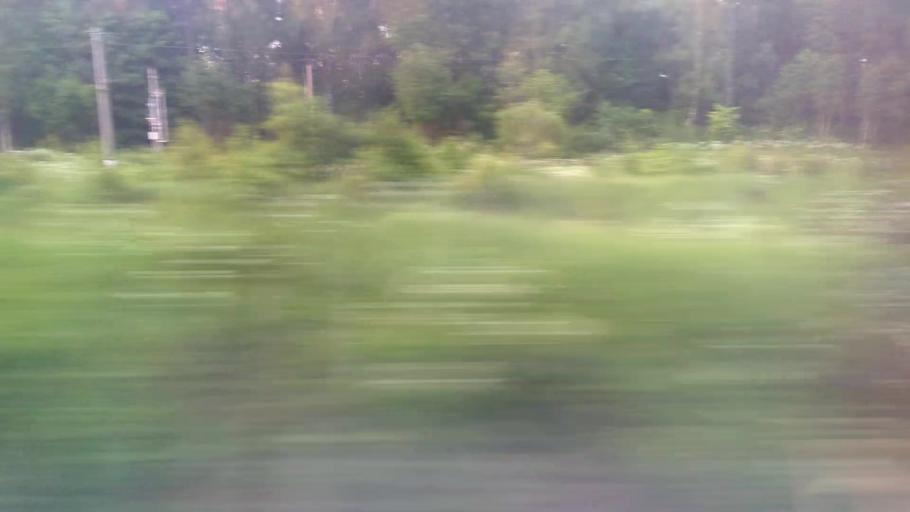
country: RU
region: Moskovskaya
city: Barybino
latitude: 55.2969
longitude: 37.8813
